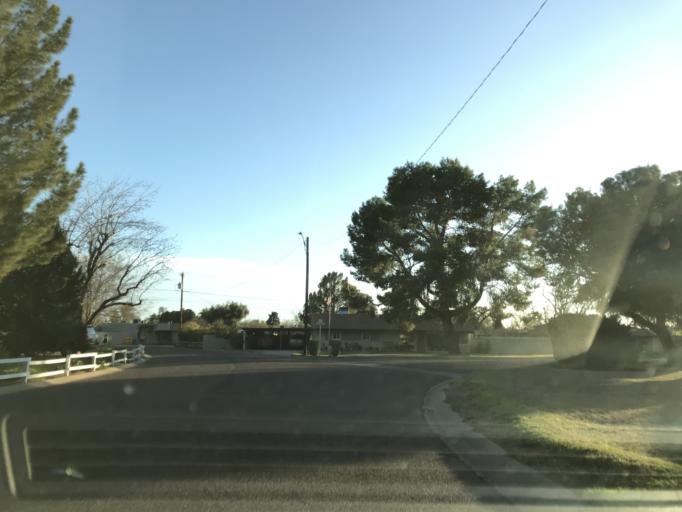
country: US
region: Arizona
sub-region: Maricopa County
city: Phoenix
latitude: 33.5213
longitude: -112.0879
